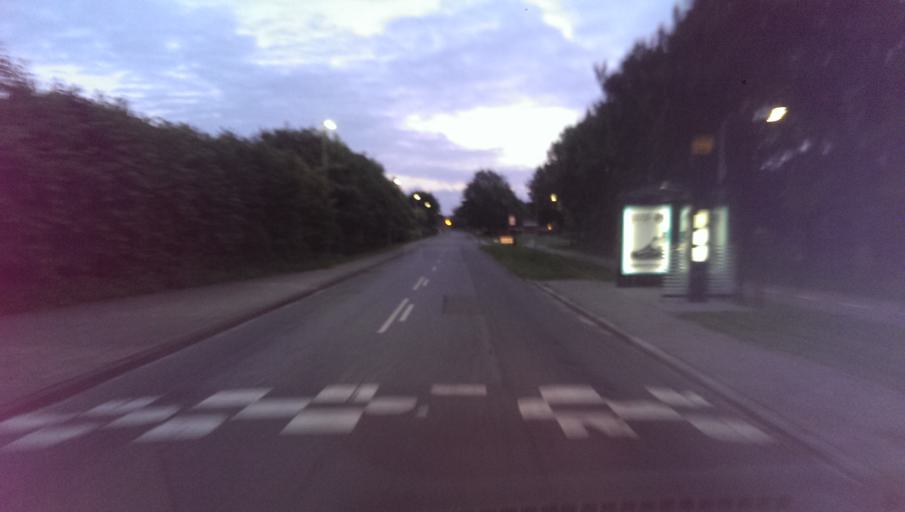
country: DK
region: South Denmark
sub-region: Esbjerg Kommune
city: Esbjerg
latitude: 55.5293
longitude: 8.4658
